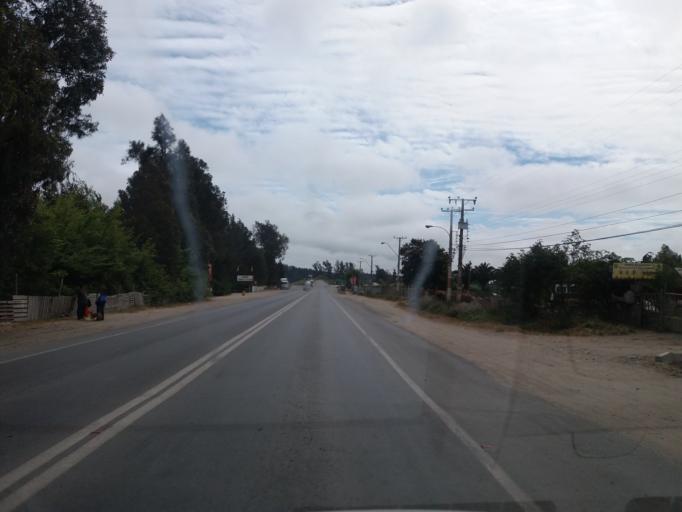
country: CL
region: Valparaiso
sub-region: Provincia de Marga Marga
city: Quilpue
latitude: -32.9303
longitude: -71.4330
